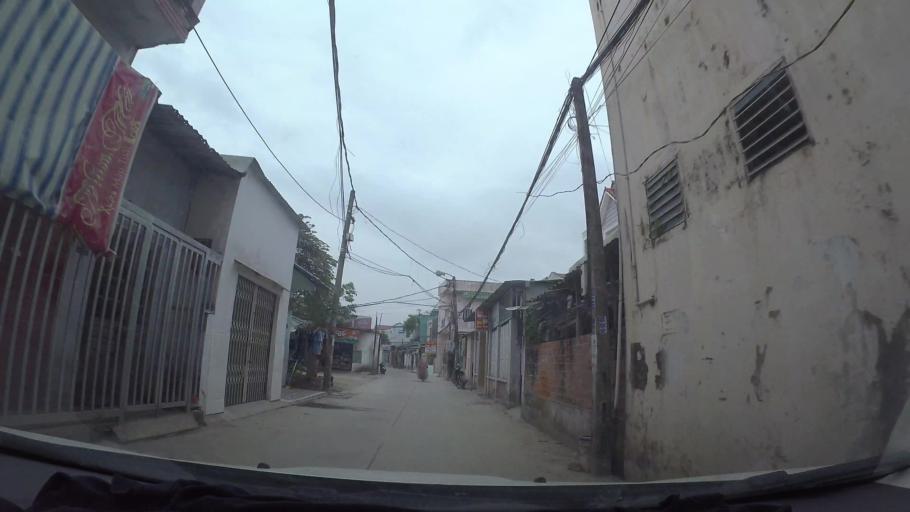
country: VN
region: Da Nang
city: Lien Chieu
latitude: 16.0875
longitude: 108.1436
